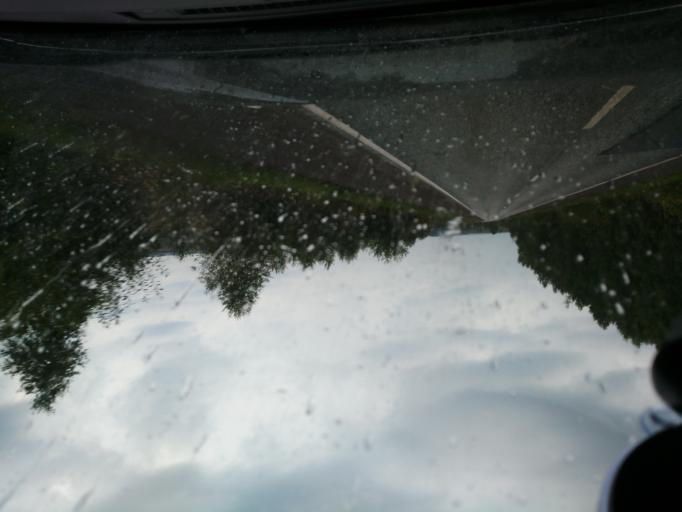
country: RU
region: Perm
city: Chernushka
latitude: 56.8482
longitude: 55.9562
